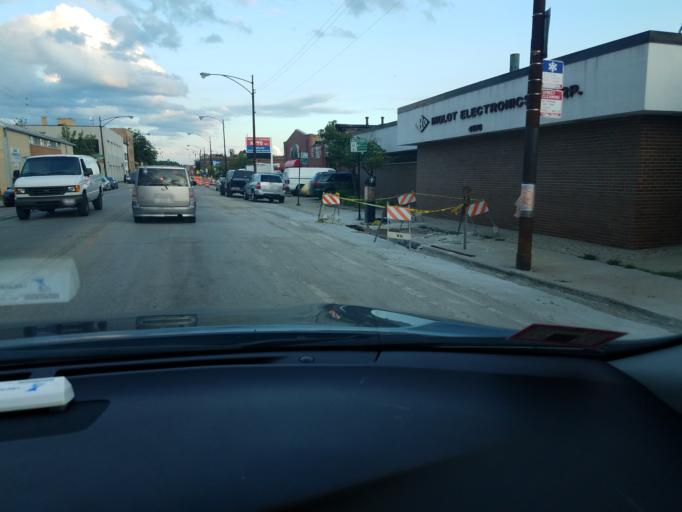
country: US
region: Illinois
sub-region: Cook County
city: Lincolnwood
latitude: 41.9695
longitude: -87.7424
